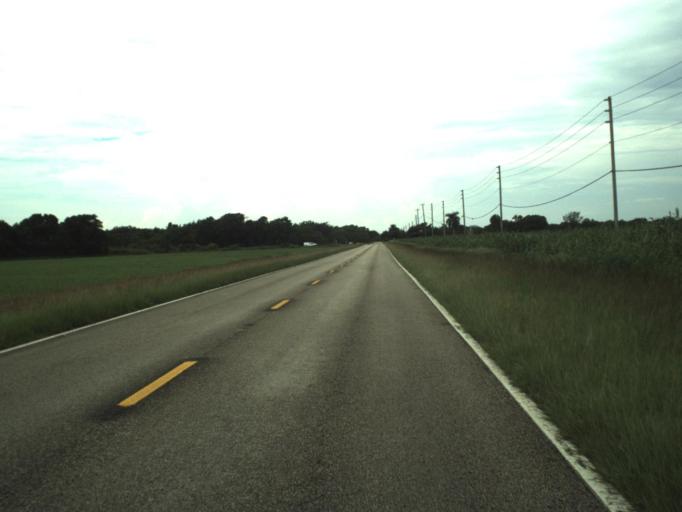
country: US
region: Florida
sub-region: Miami-Dade County
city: Florida City
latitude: 25.4107
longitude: -80.5208
